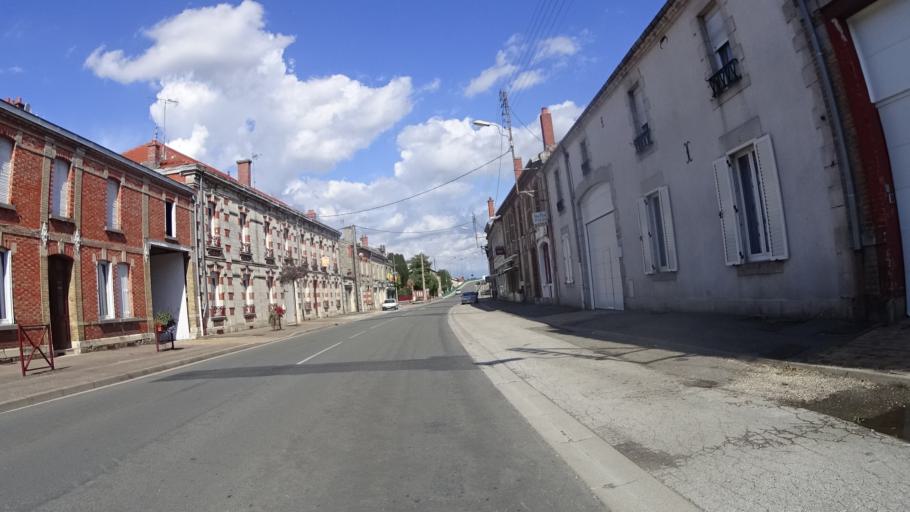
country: FR
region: Champagne-Ardenne
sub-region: Departement de la Marne
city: Pargny-sur-Saulx
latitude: 48.7688
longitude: 4.8374
